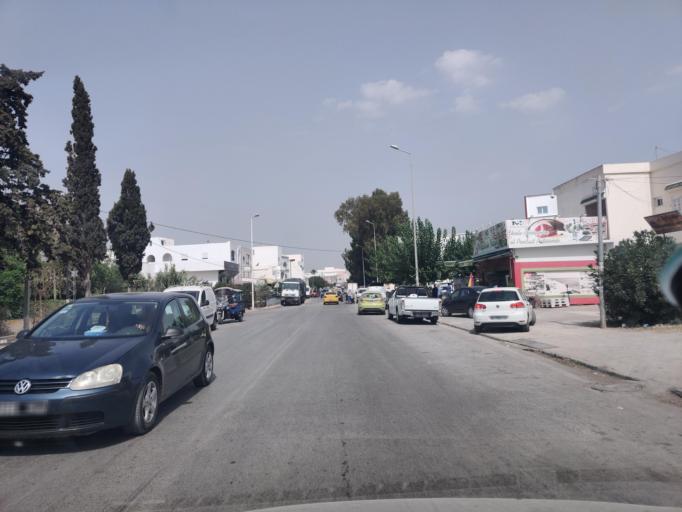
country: TN
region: Nabul
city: Al Hammamat
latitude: 36.4102
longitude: 10.6016
